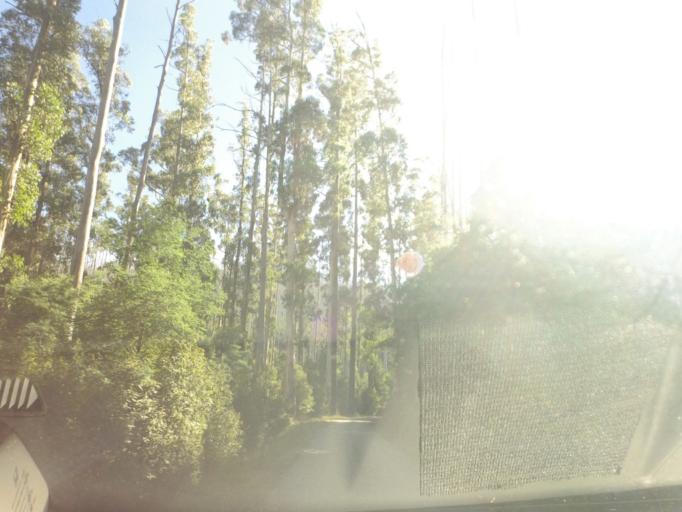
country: AU
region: Victoria
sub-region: Yarra Ranges
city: Millgrove
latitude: -37.5023
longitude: 145.8122
